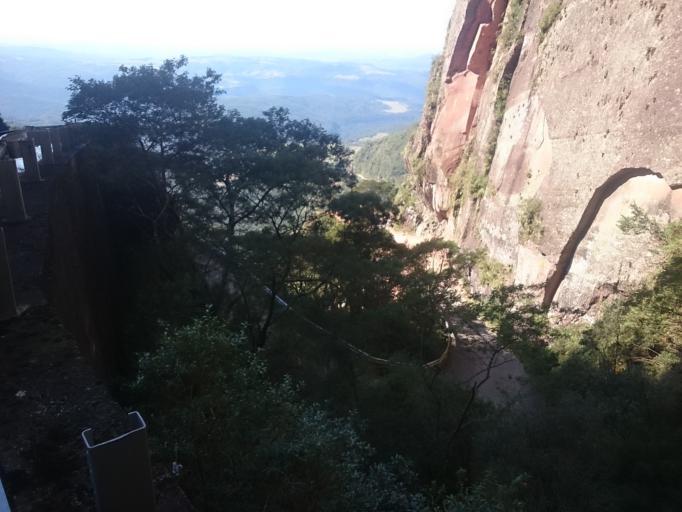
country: BR
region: Santa Catarina
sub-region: Braco Do Norte
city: Sao Jose
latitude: -28.0565
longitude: -49.3668
